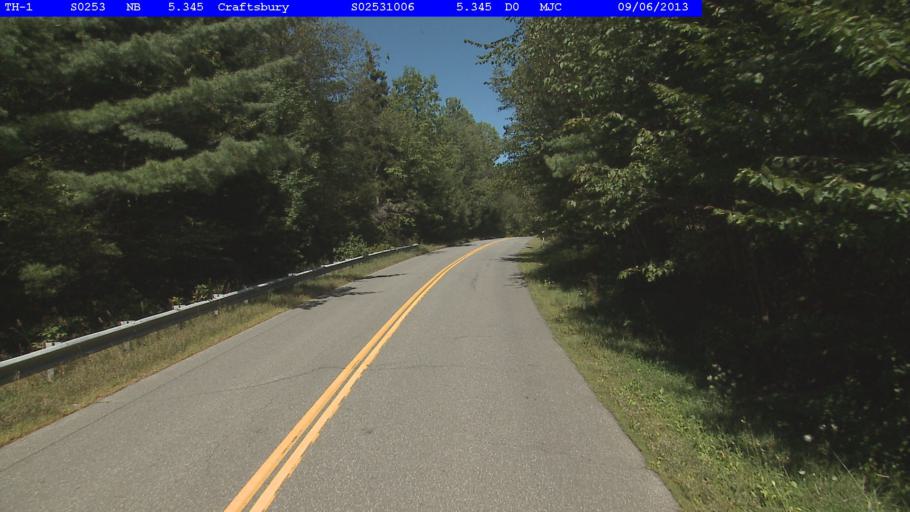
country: US
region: Vermont
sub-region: Caledonia County
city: Hardwick
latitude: 44.6787
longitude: -72.4032
